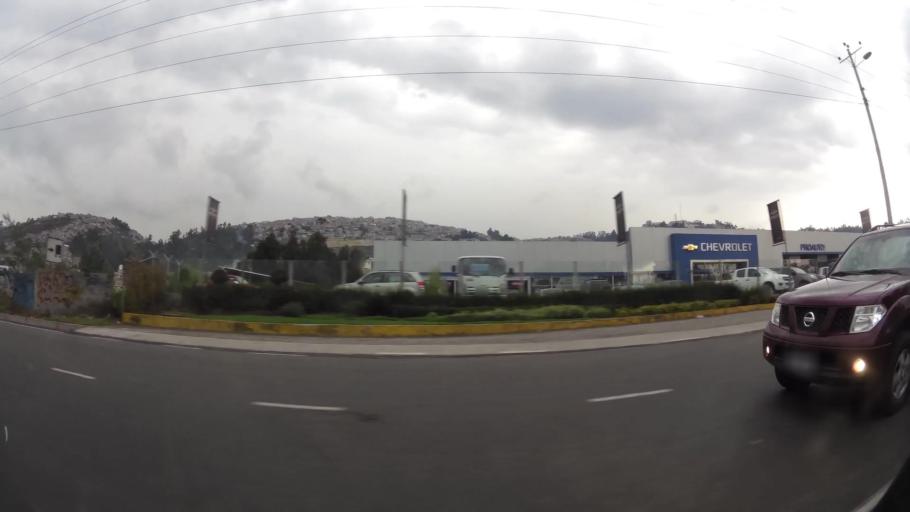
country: EC
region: Pichincha
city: Quito
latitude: -0.1130
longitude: -78.4572
